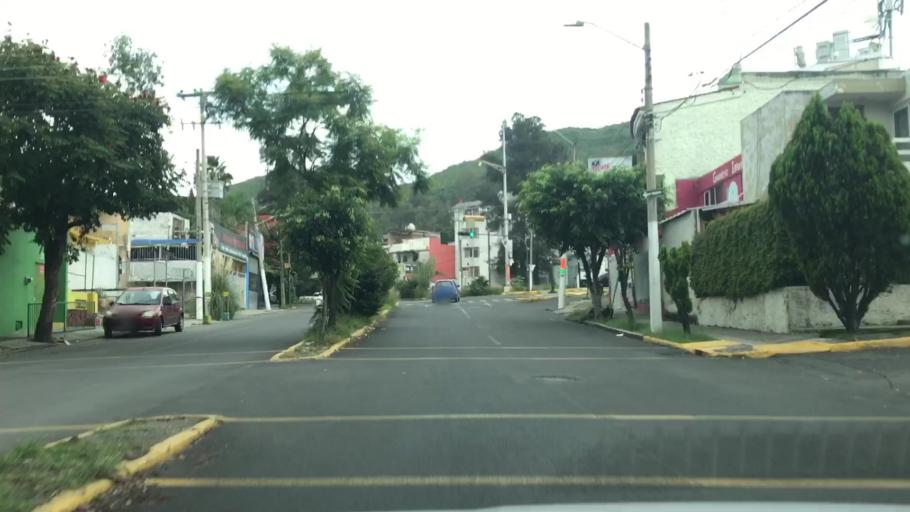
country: MX
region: Jalisco
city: Guadalajara
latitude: 20.6219
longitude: -103.4091
